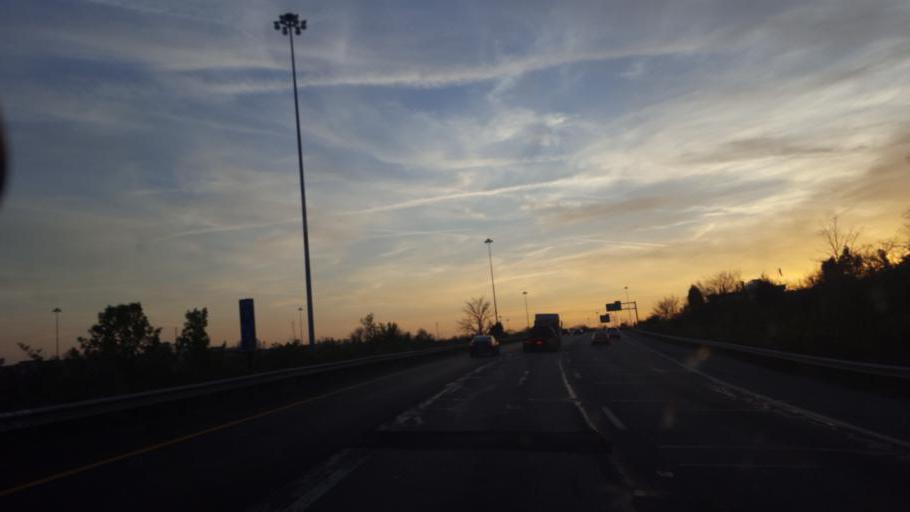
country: US
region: Ohio
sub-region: Hamilton County
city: Golf Manor
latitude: 39.1655
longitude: -84.4272
